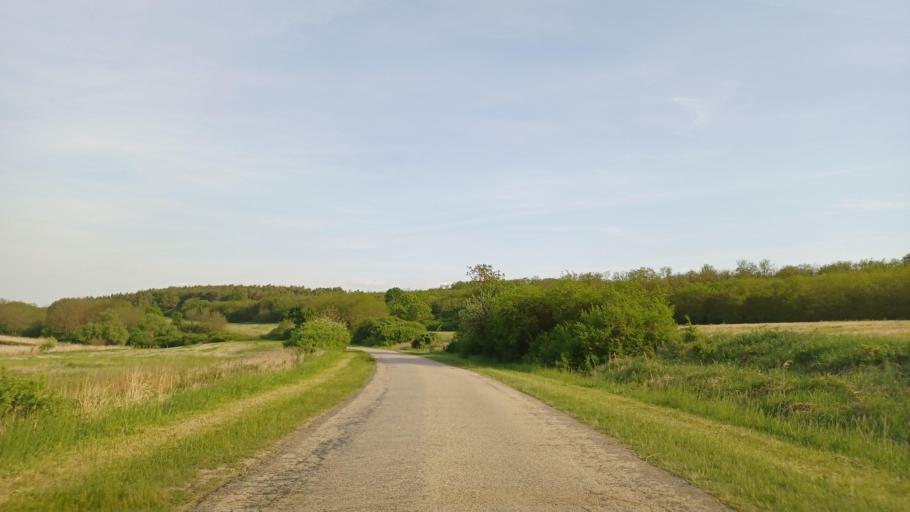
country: HU
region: Baranya
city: Kozarmisleny
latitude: 45.9655
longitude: 18.3672
